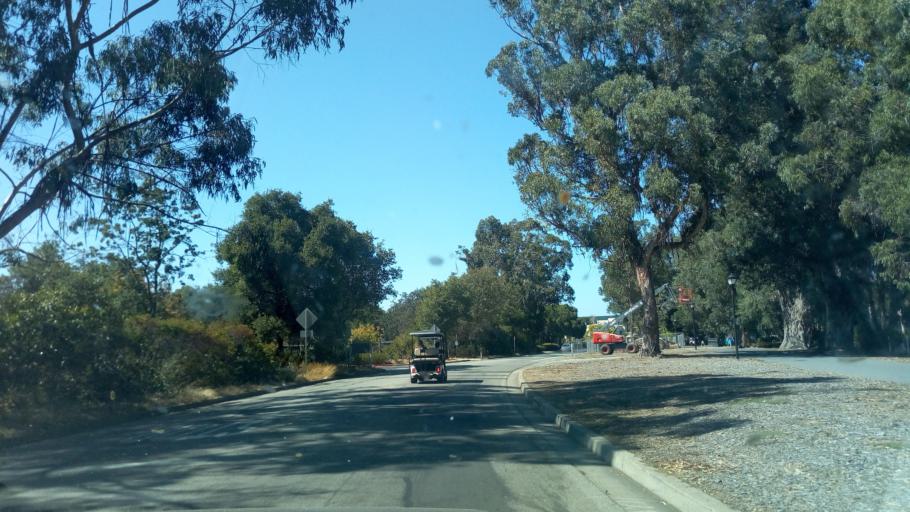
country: US
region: California
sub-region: Santa Clara County
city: Stanford
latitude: 37.4287
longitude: -122.1781
